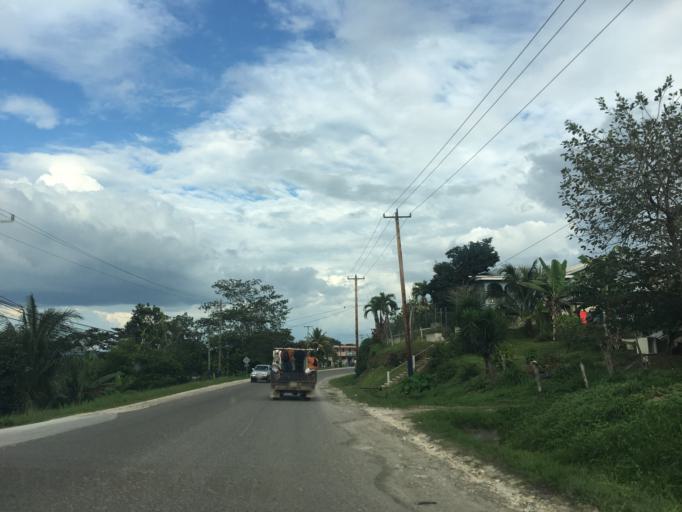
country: BZ
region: Cayo
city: San Ignacio
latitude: 17.1481
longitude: -89.0794
